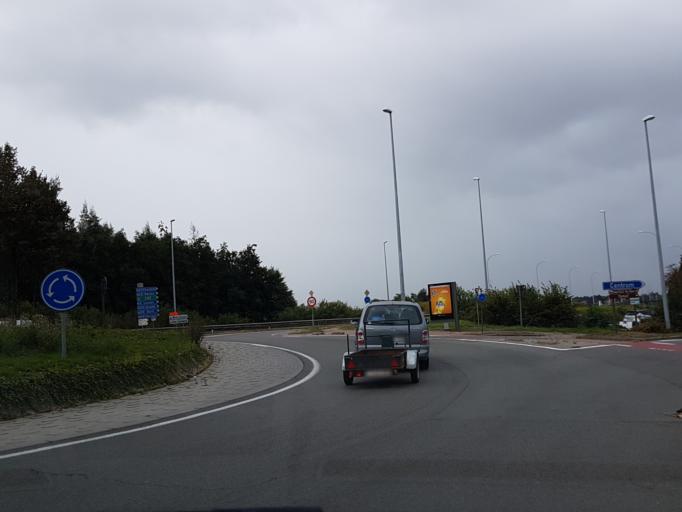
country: BE
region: Flanders
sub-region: Provincie Vlaams-Brabant
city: Tienen
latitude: 50.7994
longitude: 4.9718
